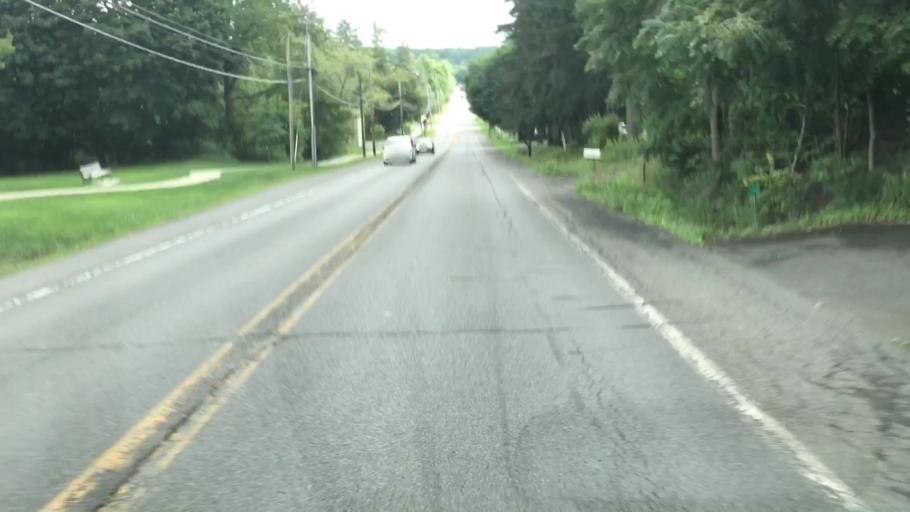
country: US
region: New York
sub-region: Onondaga County
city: Skaneateles
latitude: 42.9443
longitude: -76.4428
